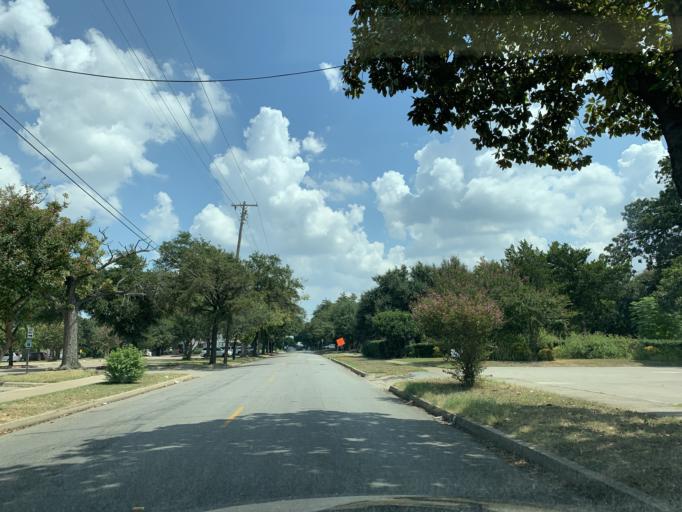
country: US
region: Texas
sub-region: Dallas County
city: Dallas
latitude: 32.7420
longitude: -96.8221
